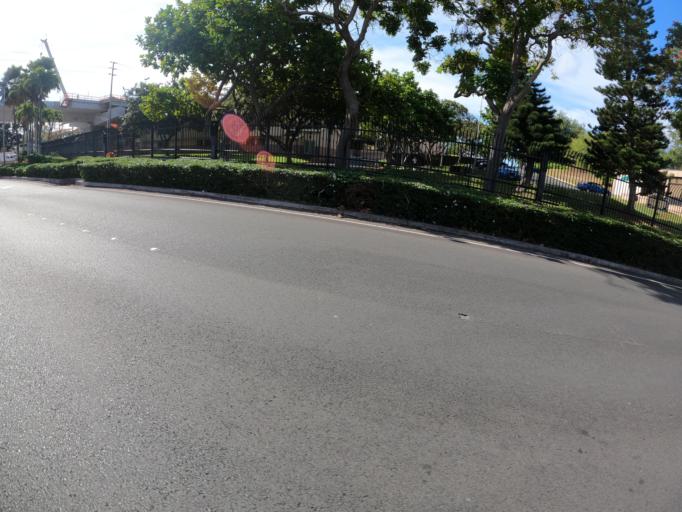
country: US
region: Hawaii
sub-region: Honolulu County
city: Hickam Field
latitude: 21.3526
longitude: -157.9363
